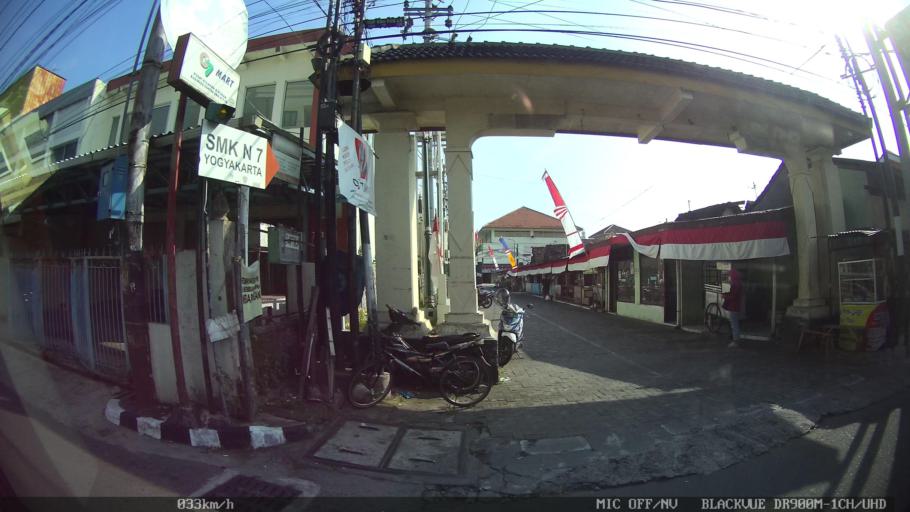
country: ID
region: Daerah Istimewa Yogyakarta
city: Yogyakarta
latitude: -7.7874
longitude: 110.3647
